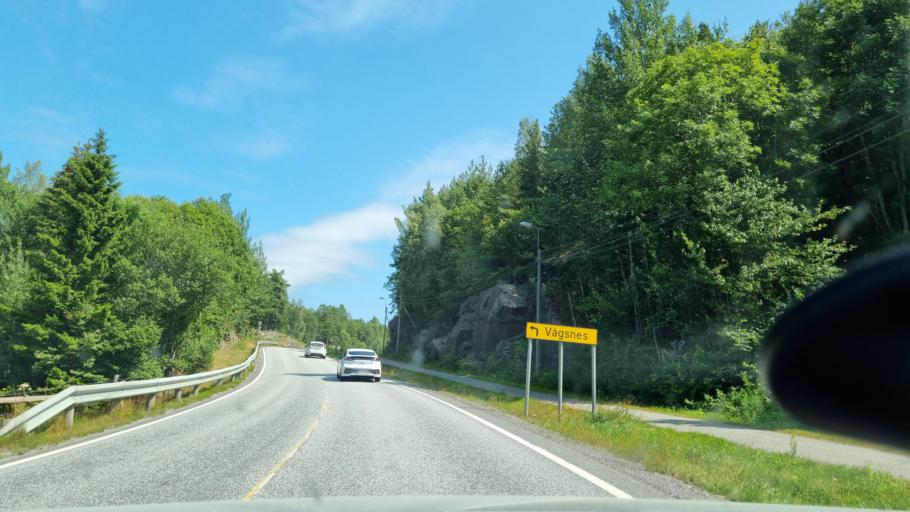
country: NO
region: Aust-Agder
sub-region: Arendal
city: Arendal
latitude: 58.4675
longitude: 8.8452
